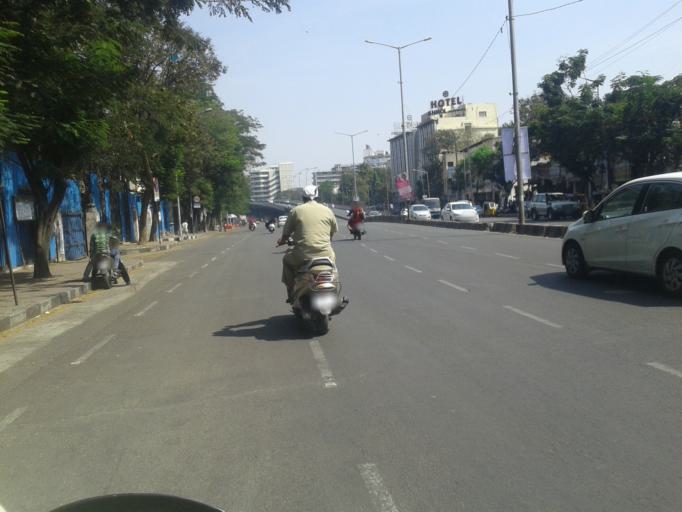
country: IN
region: Telangana
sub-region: Hyderabad
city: Hyderabad
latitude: 17.4079
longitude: 78.4687
